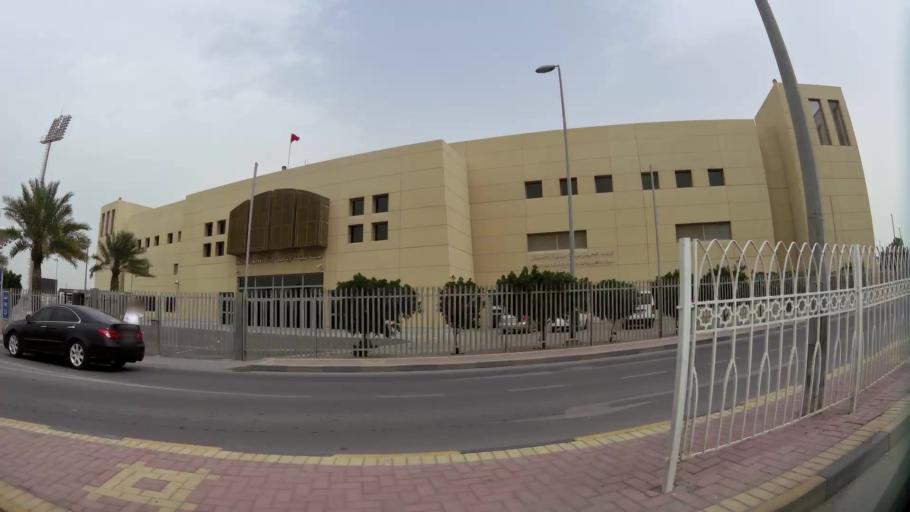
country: BH
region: Northern
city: Madinat `Isa
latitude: 26.1734
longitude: 50.5486
